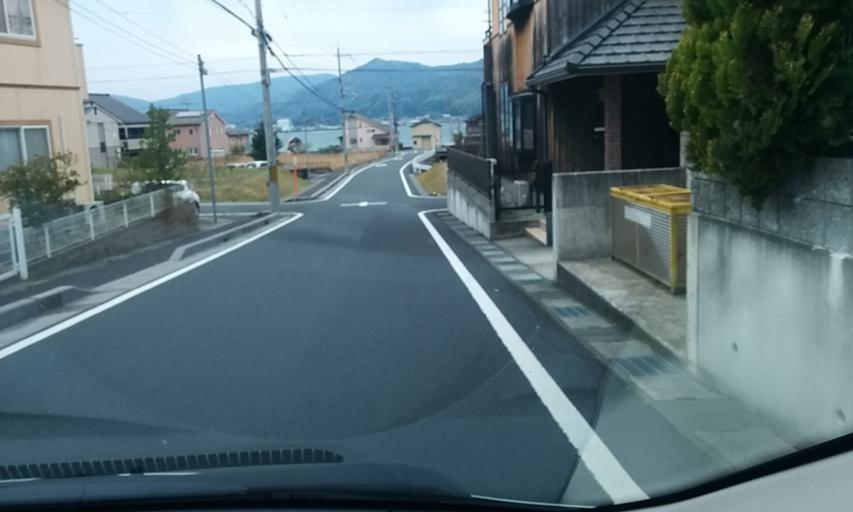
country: JP
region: Kyoto
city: Miyazu
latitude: 35.5539
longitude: 135.2108
